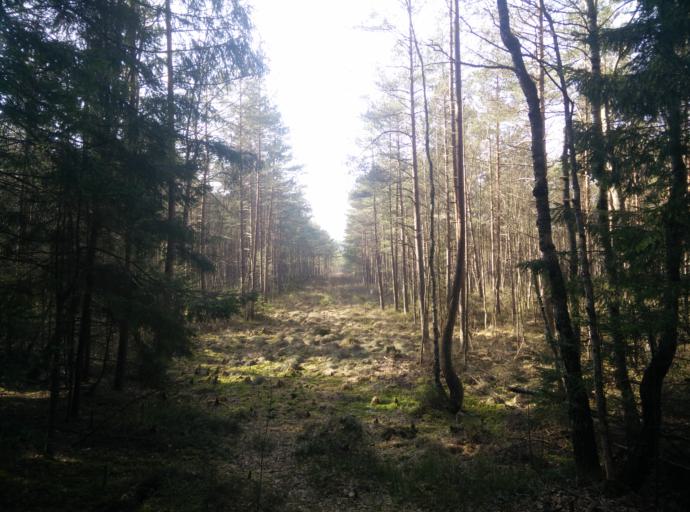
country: LT
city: Trakai
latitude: 54.6442
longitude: 24.9747
